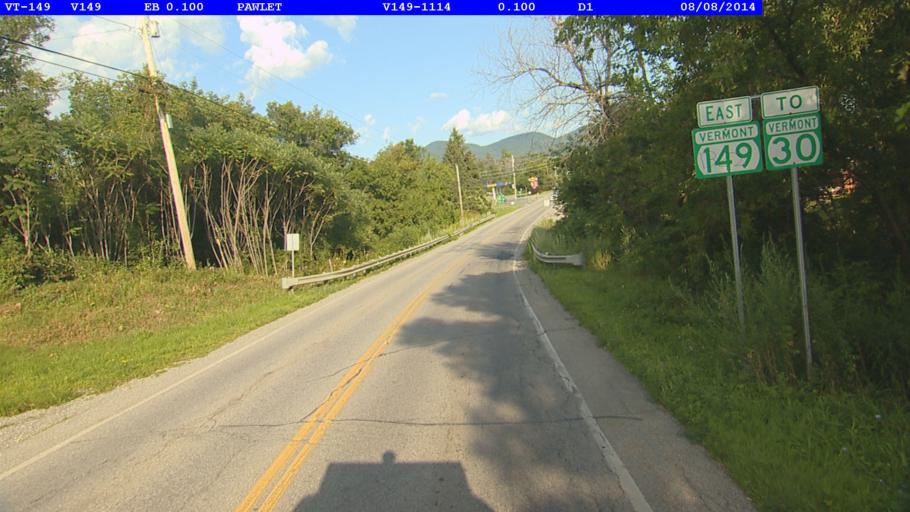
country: US
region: New York
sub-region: Washington County
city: Granville
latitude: 43.4060
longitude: -73.2490
